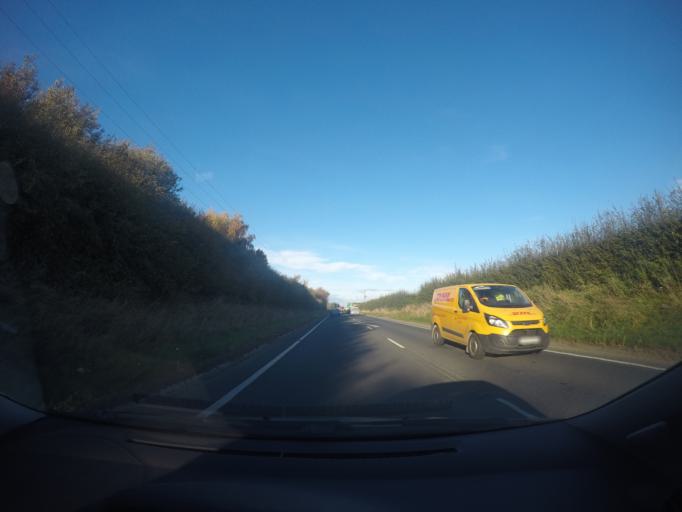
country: GB
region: England
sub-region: City of York
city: Nether Poppleton
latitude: 53.9689
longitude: -1.1459
